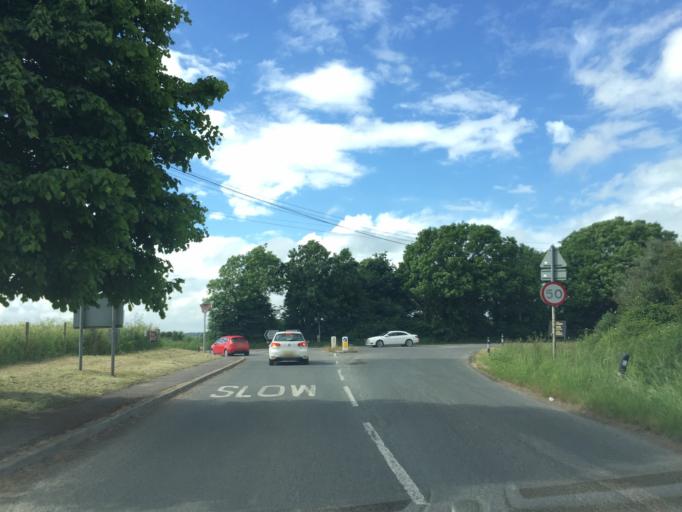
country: GB
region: England
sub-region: Dorset
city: Bovington Camp
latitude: 50.6670
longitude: -2.2775
